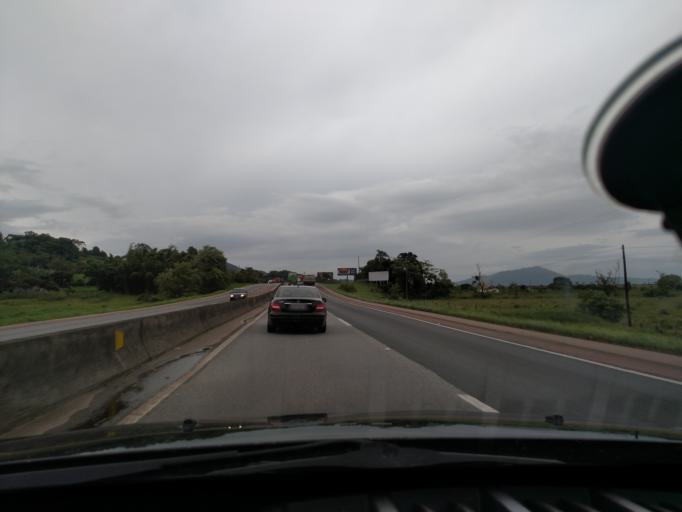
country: BR
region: Santa Catarina
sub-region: Tijucas
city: Tijucas
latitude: -27.3267
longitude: -48.6268
